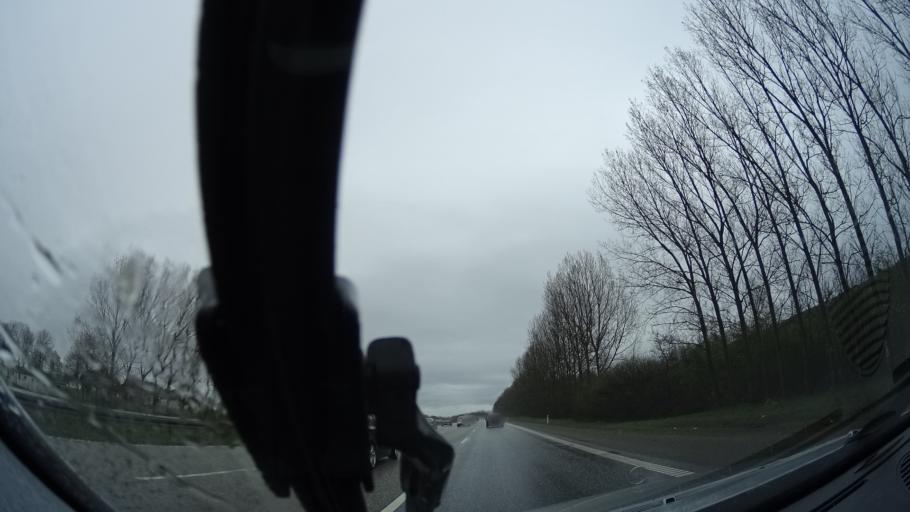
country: DK
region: Capital Region
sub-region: Hoje-Taastrup Kommune
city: Taastrup
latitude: 55.6649
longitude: 12.2677
